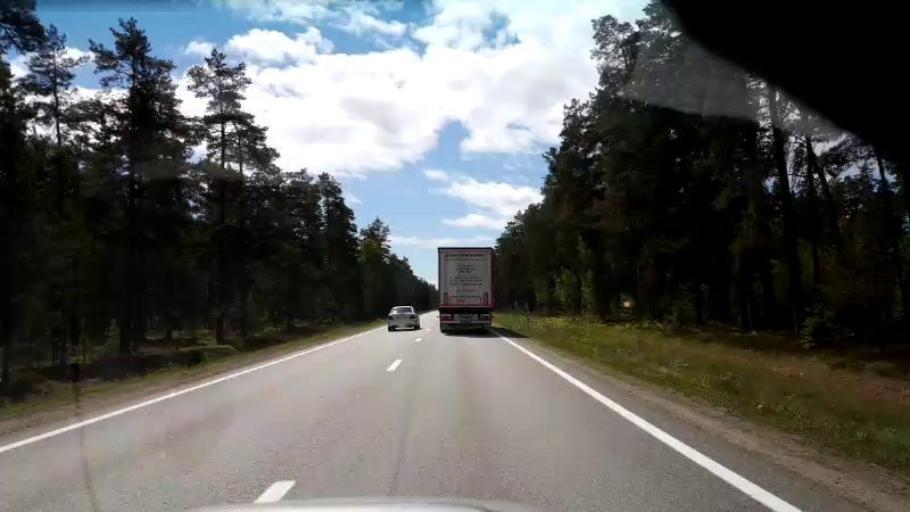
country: LV
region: Salacgrivas
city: Salacgriva
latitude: 57.5543
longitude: 24.4332
